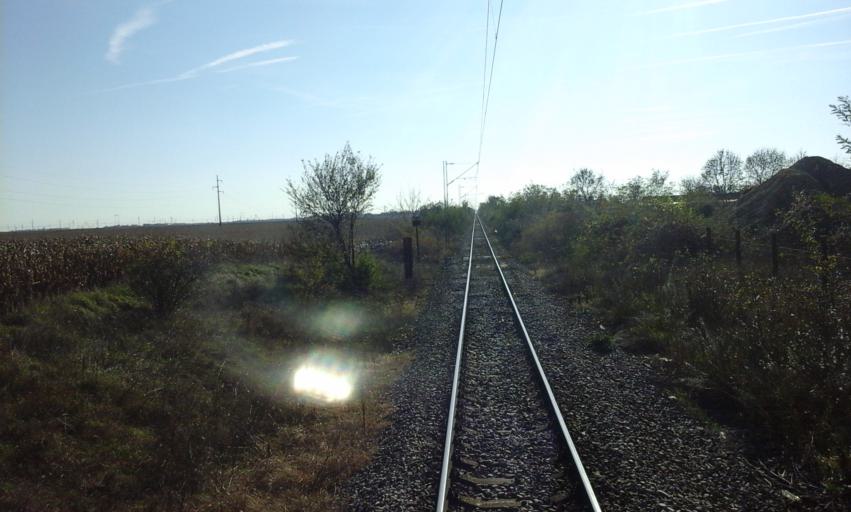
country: RS
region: Autonomna Pokrajina Vojvodina
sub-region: Severnobacki Okrug
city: Subotica
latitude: 46.0557
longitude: 19.6862
